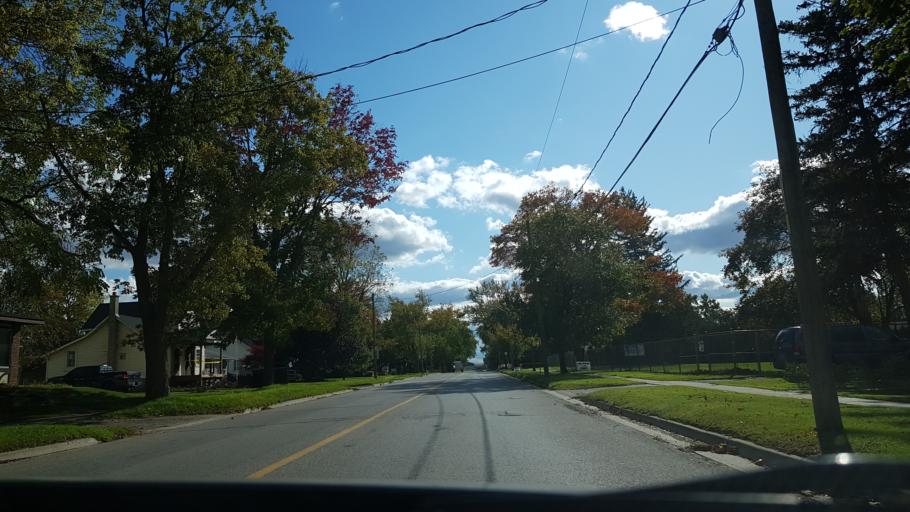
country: CA
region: Ontario
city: South Huron
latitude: 43.1578
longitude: -81.6855
